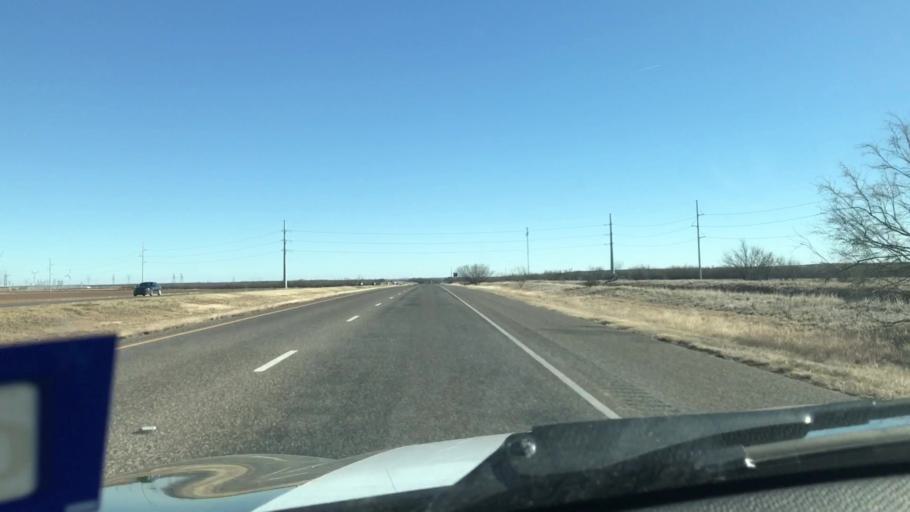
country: US
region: Texas
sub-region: Scurry County
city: Snyder
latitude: 32.8670
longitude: -101.0337
